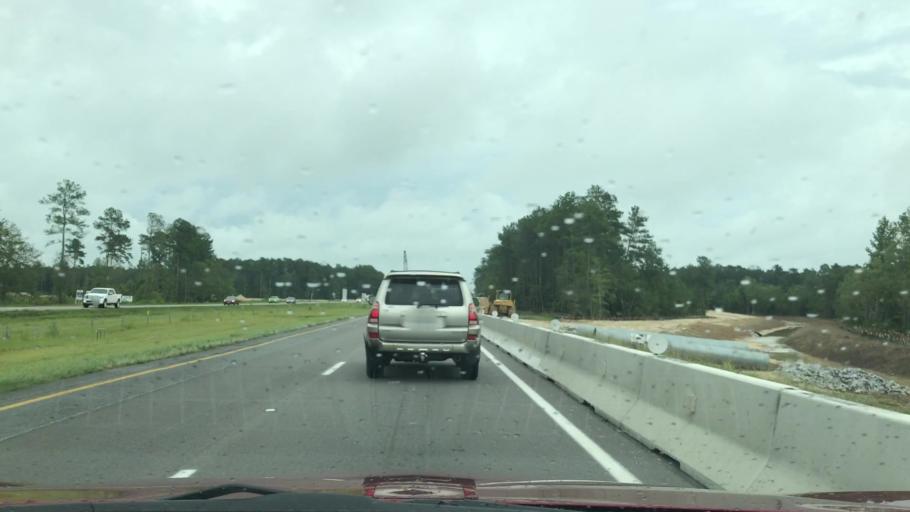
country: US
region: South Carolina
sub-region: Dorchester County
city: Ridgeville
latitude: 33.1231
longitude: -80.2816
